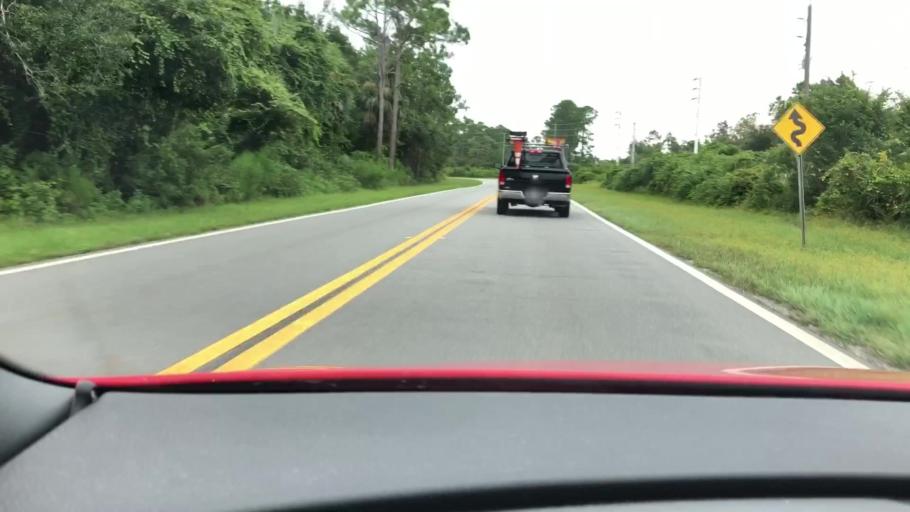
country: US
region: Florida
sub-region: Flagler County
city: Palm Coast
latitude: 29.5119
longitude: -81.1952
